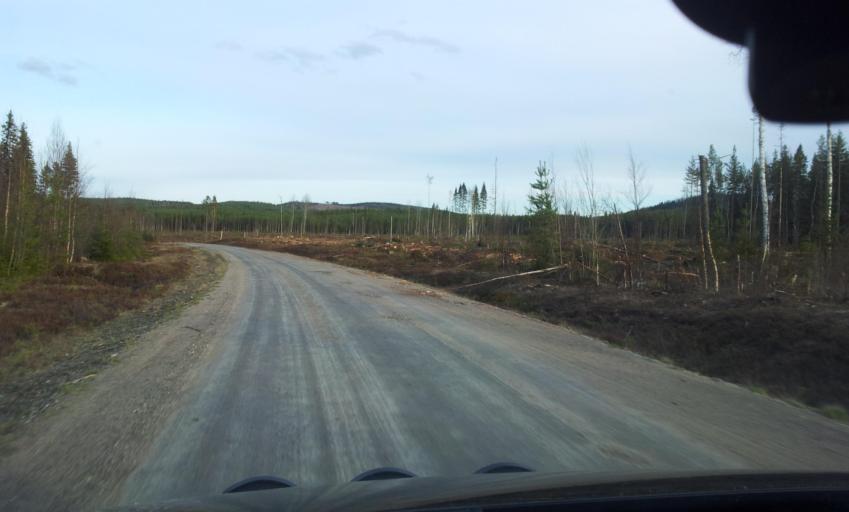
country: SE
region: Gaevleborg
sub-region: Ljusdals Kommun
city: Farila
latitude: 62.1240
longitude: 15.6717
